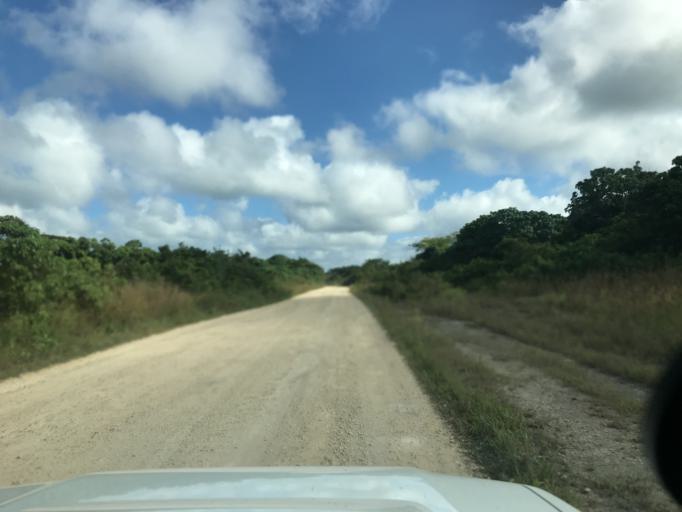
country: VU
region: Sanma
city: Luganville
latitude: -15.5120
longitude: 167.1276
